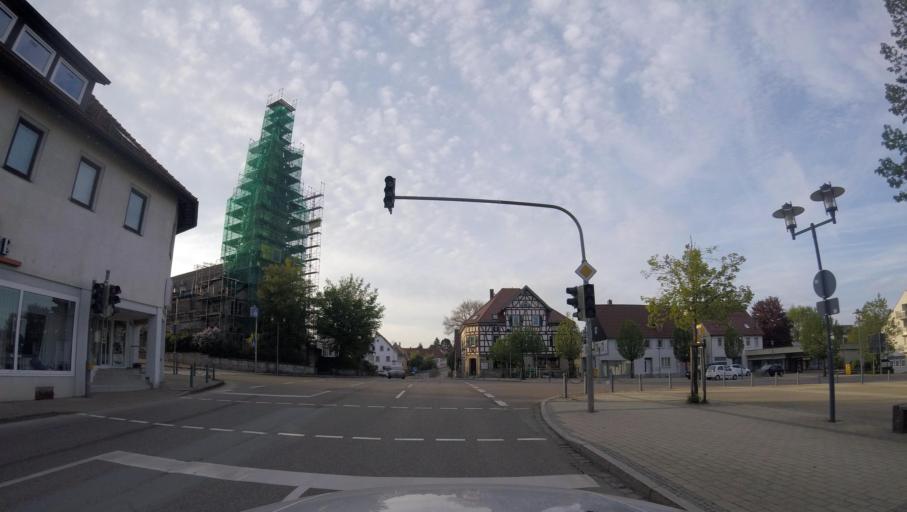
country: DE
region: Baden-Wuerttemberg
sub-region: Regierungsbezirk Stuttgart
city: Gschwend
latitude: 48.9339
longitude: 9.7433
